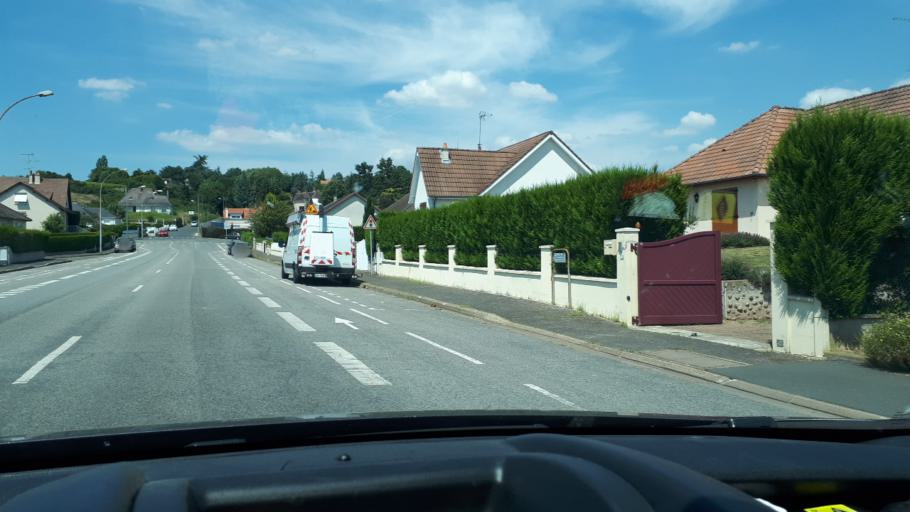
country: FR
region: Centre
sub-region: Departement du Loir-et-Cher
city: Vendome
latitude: 47.8067
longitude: 1.0532
